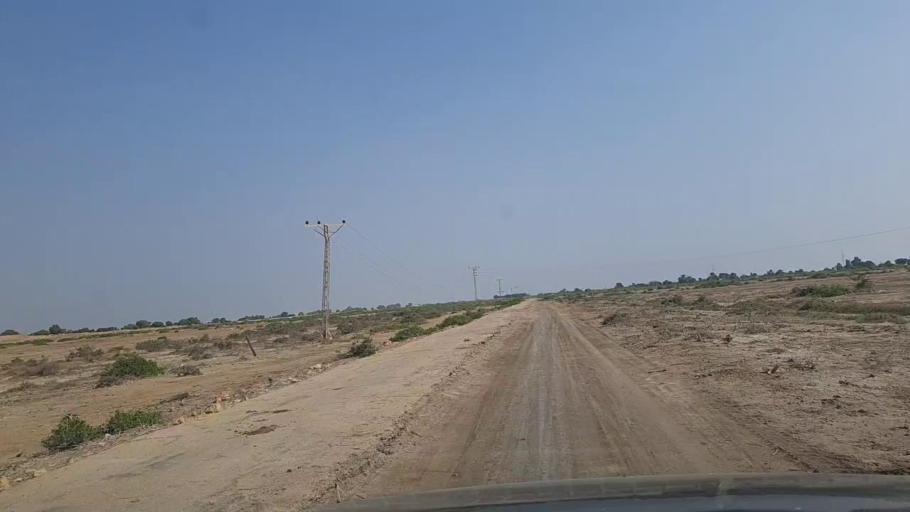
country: PK
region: Sindh
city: Gharo
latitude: 24.7413
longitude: 67.6492
